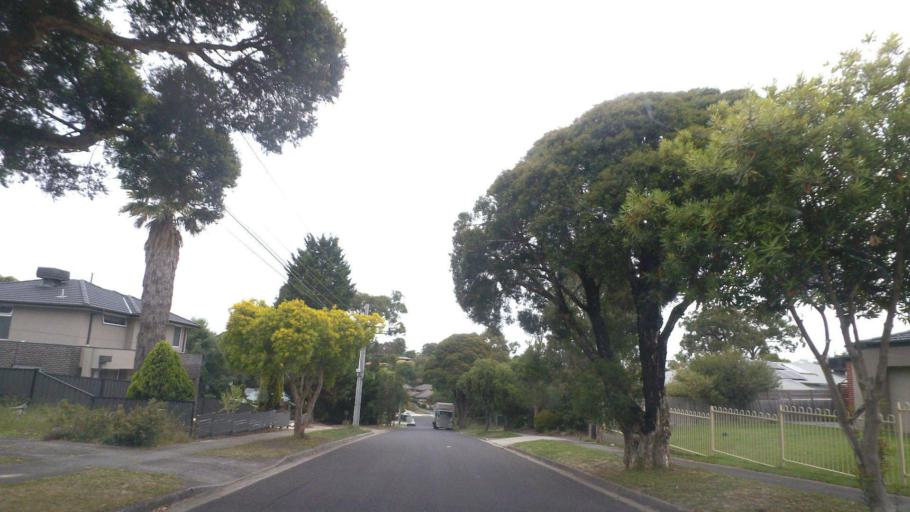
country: AU
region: Victoria
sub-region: Knox
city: Boronia
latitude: -37.8624
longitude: 145.2716
